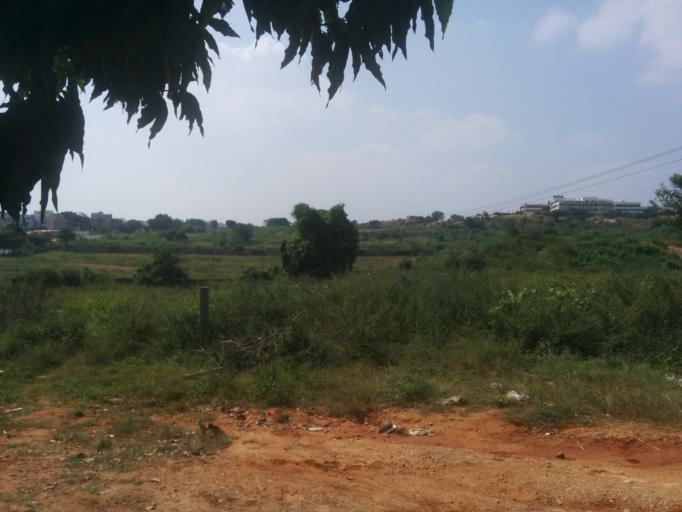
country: IN
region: Karnataka
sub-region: Bangalore Urban
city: Bangalore
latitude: 12.9040
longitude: 77.5352
